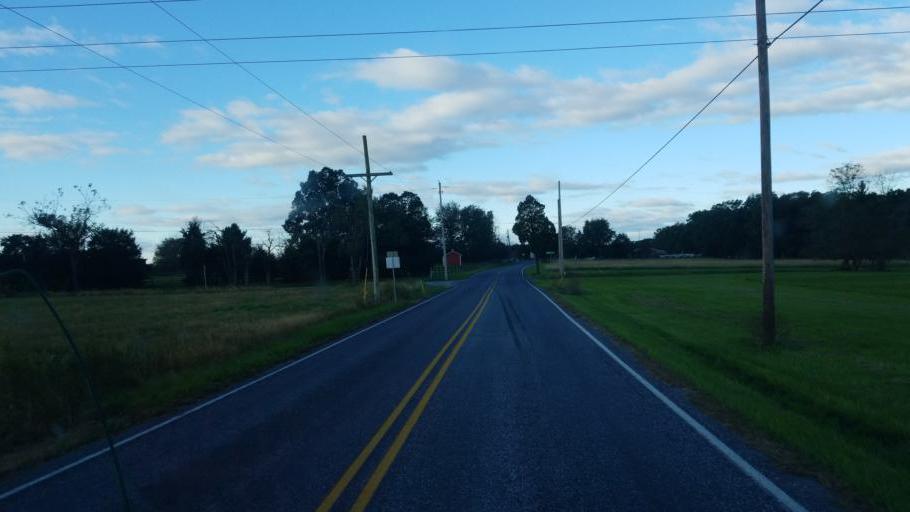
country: US
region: Pennsylvania
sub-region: Adams County
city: New Oxford
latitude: 39.8924
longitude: -77.1177
